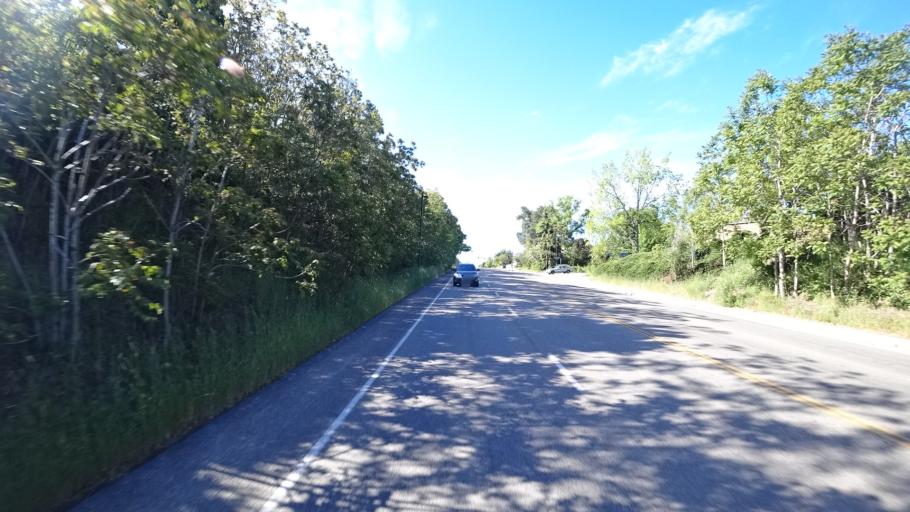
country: US
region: Idaho
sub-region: Ada County
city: Garden City
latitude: 43.5872
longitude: -116.2436
